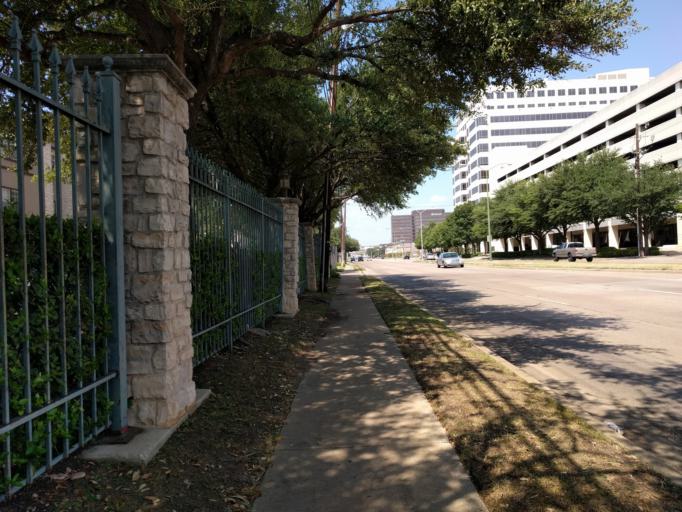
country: US
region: Texas
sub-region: Dallas County
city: Richardson
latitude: 32.9160
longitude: -96.7693
